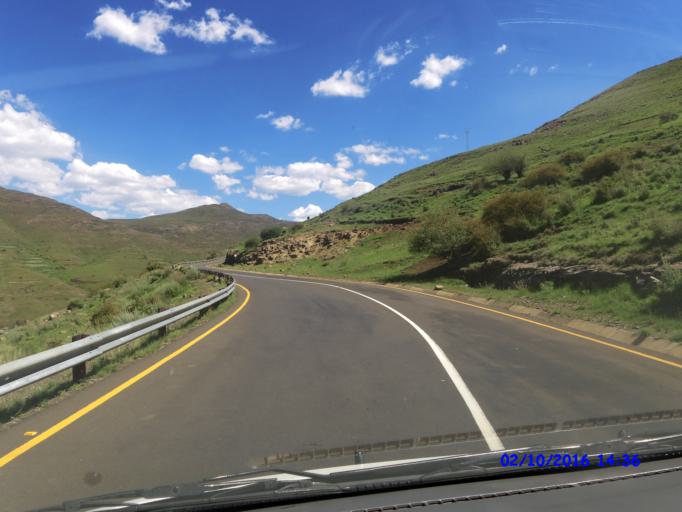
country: LS
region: Maseru
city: Nako
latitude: -29.4954
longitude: 28.0620
